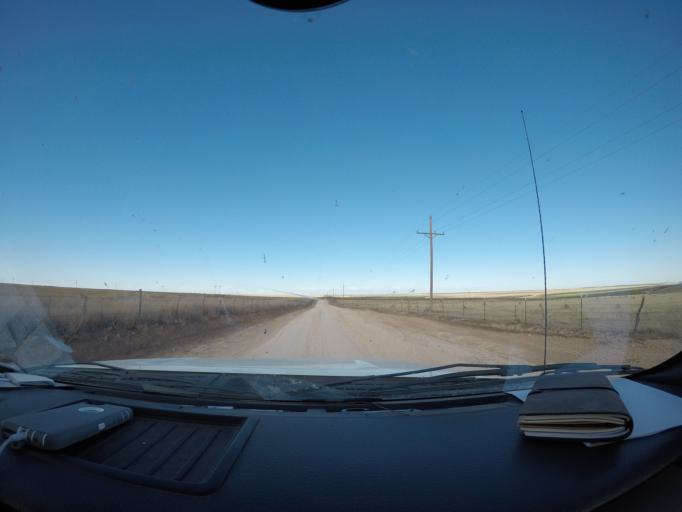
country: US
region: Texas
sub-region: Parmer County
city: Bovina
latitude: 34.6299
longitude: -103.0911
